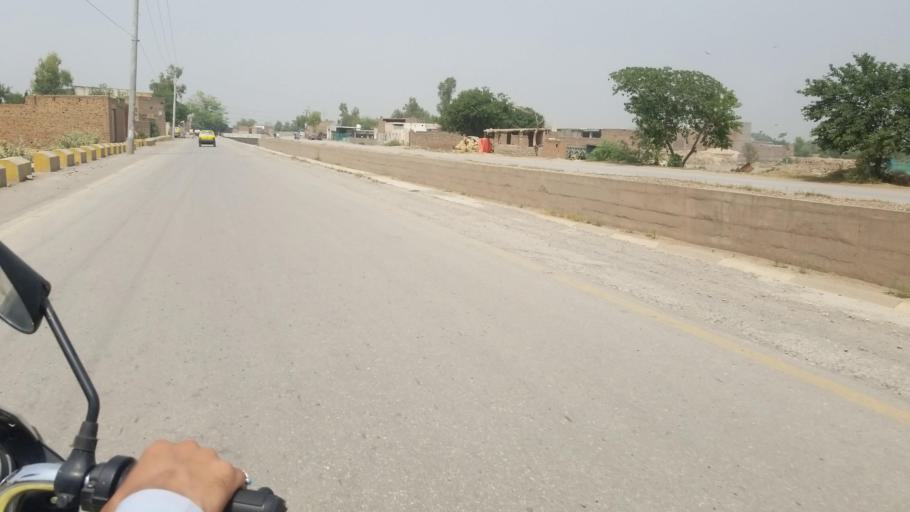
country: PK
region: Khyber Pakhtunkhwa
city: Peshawar
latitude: 33.9593
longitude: 71.5457
